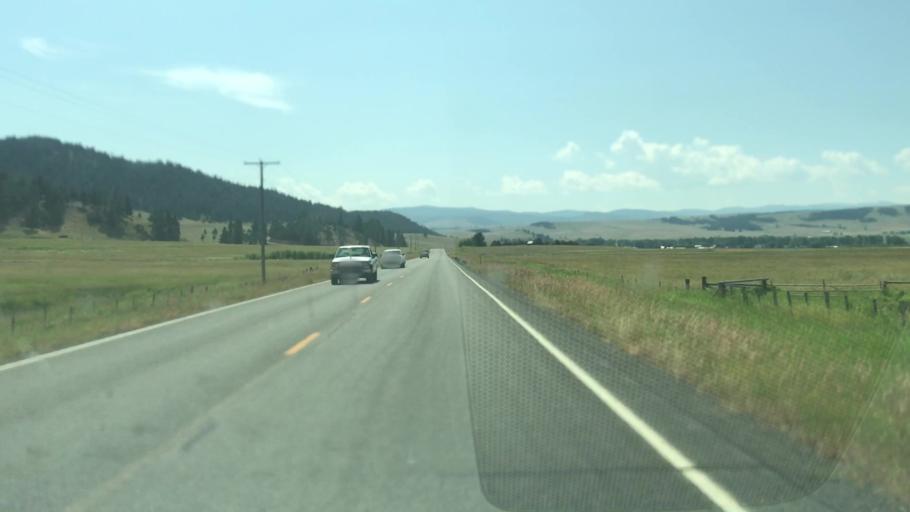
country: US
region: Montana
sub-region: Powell County
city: Deer Lodge
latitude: 46.6155
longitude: -112.6098
